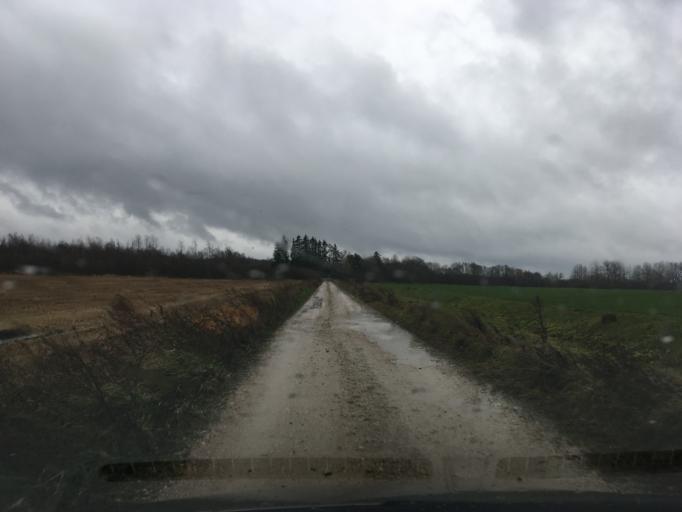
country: EE
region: Laeaene
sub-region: Lihula vald
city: Lihula
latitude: 58.7026
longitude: 23.8553
